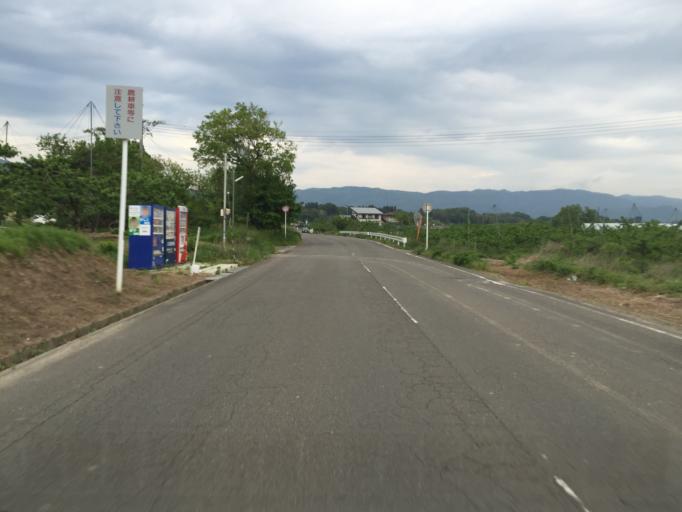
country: JP
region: Fukushima
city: Hobaramachi
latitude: 37.8425
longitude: 140.5376
